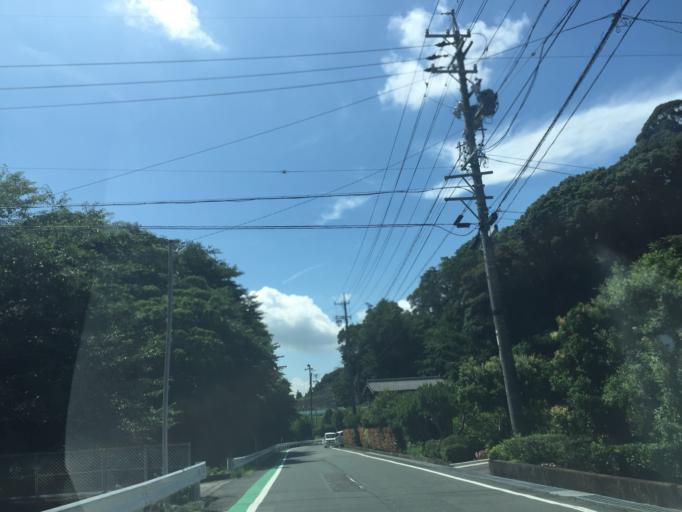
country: JP
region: Shizuoka
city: Kakegawa
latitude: 34.7889
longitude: 138.0730
